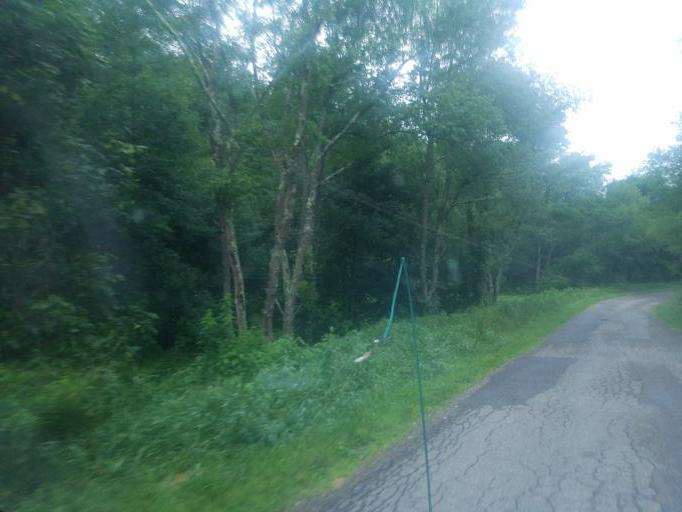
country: US
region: Ohio
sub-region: Columbiana County
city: Salineville
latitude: 40.6139
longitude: -80.8904
